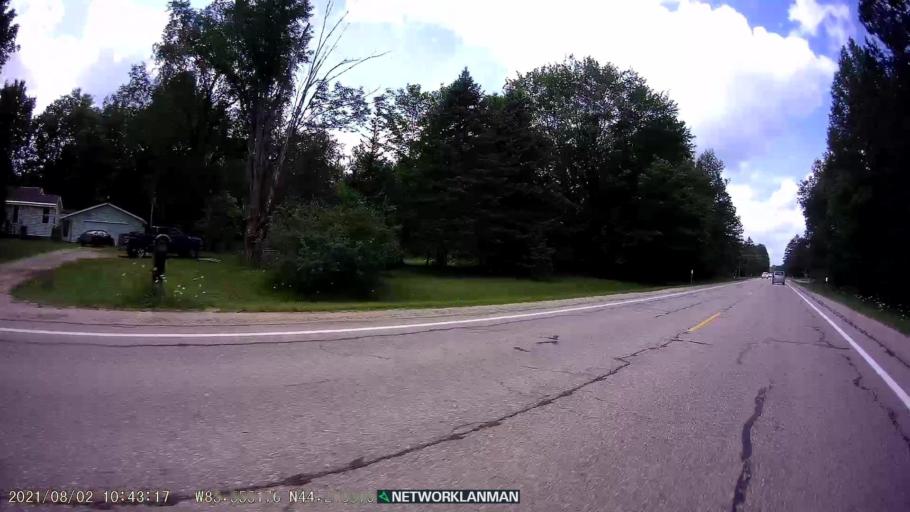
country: US
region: Michigan
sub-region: Wexford County
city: Cadillac
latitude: 44.2183
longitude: -85.5569
